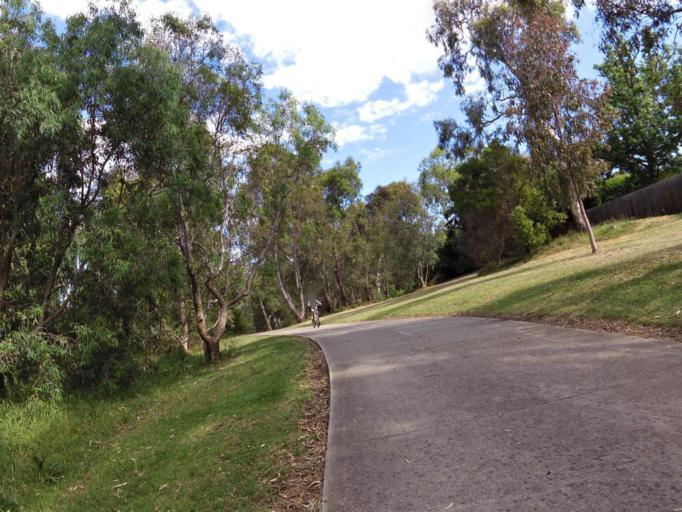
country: AU
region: Victoria
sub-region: Banyule
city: Viewbank
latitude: -37.7394
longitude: 145.0802
